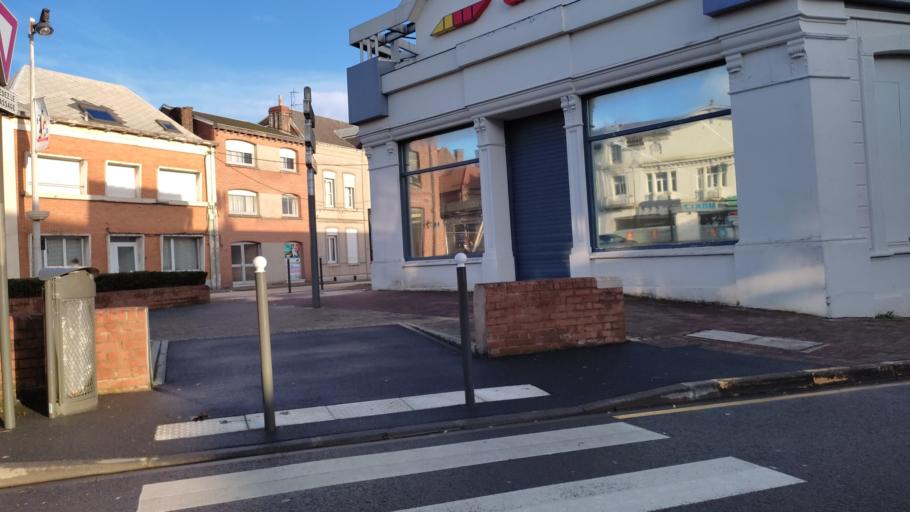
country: FR
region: Nord-Pas-de-Calais
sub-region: Departement du Pas-de-Calais
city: Bethune
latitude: 50.5279
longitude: 2.6427
